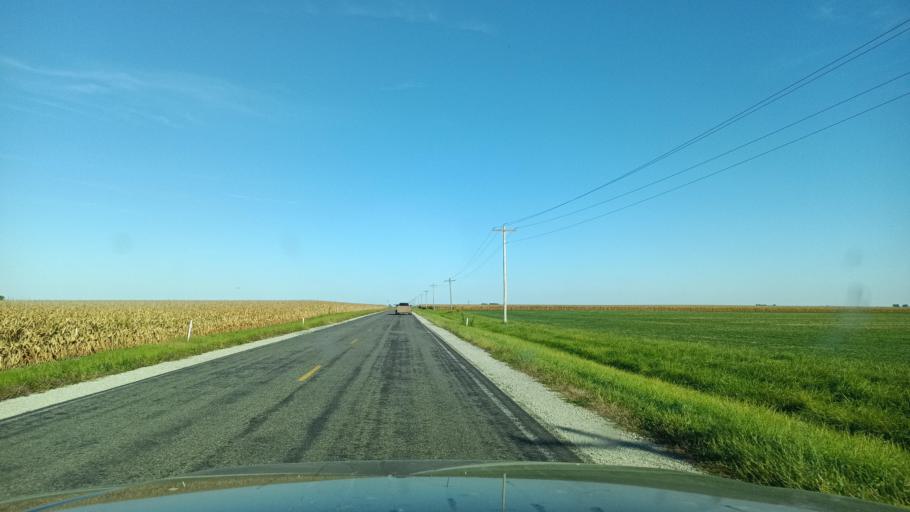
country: US
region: Illinois
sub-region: McLean County
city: Le Roy
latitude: 40.2243
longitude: -88.7960
